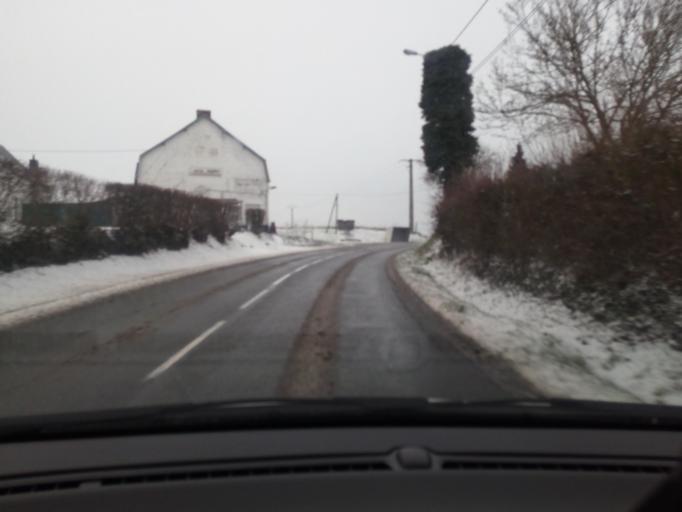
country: FR
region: Nord-Pas-de-Calais
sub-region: Departement du Nord
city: La Longueville
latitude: 50.3277
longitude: 3.8675
